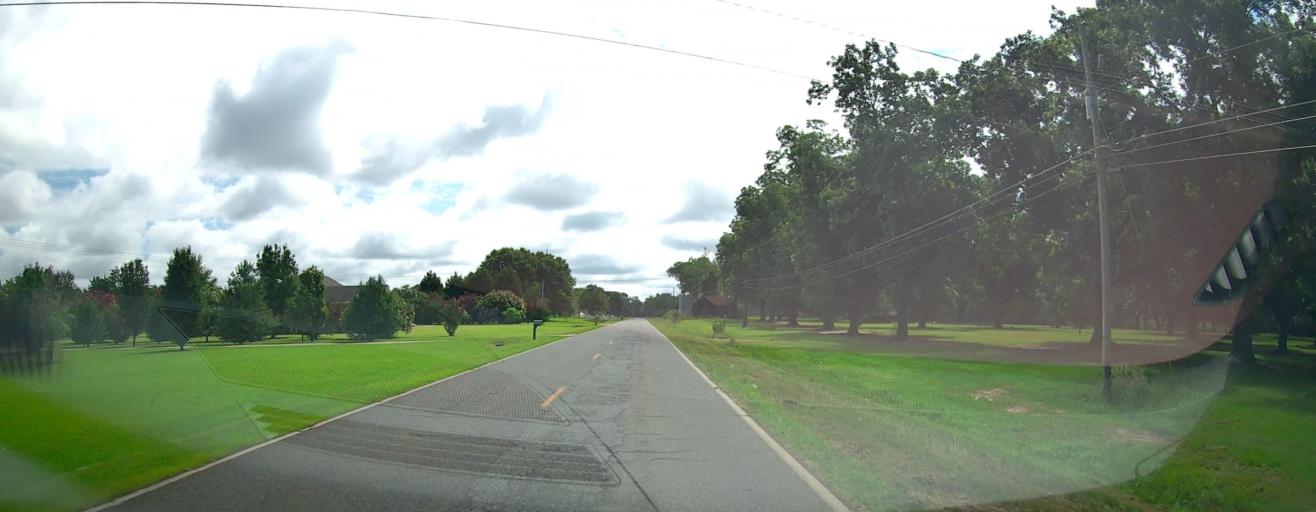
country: US
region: Georgia
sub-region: Peach County
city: Byron
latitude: 32.6456
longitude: -83.7795
